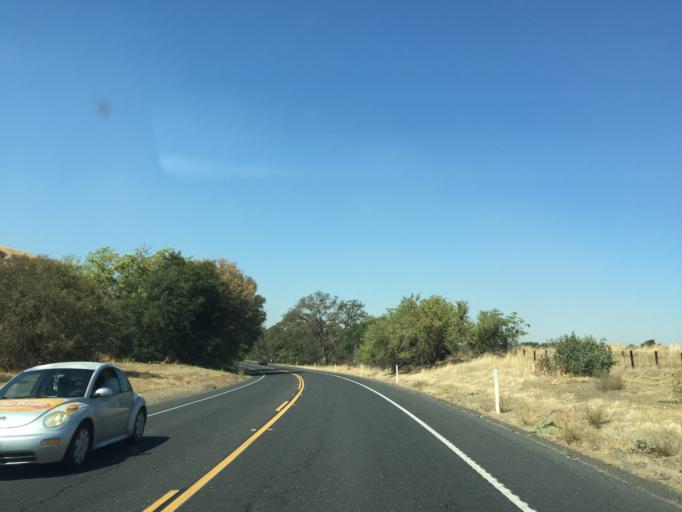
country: US
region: California
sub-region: Stanislaus County
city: East Oakdale
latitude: 37.8060
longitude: -120.6841
